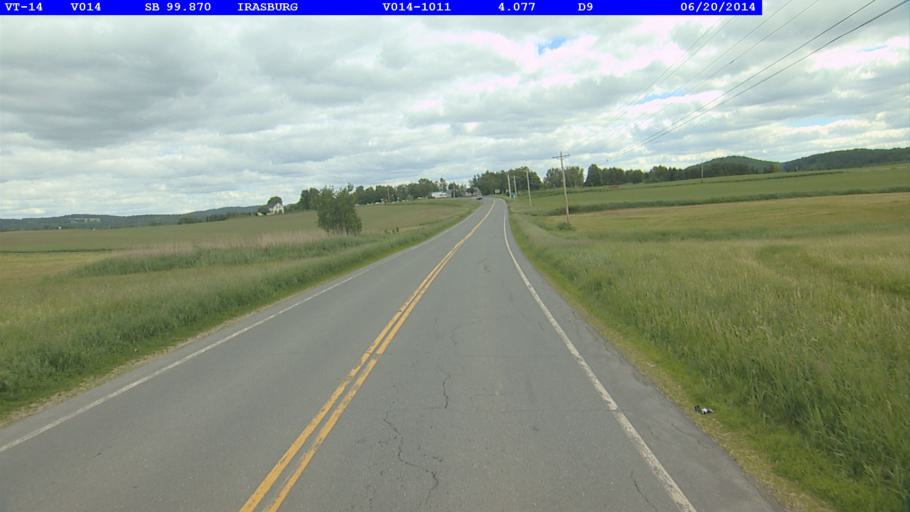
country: US
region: Vermont
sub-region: Orleans County
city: Newport
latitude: 44.8186
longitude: -72.2952
